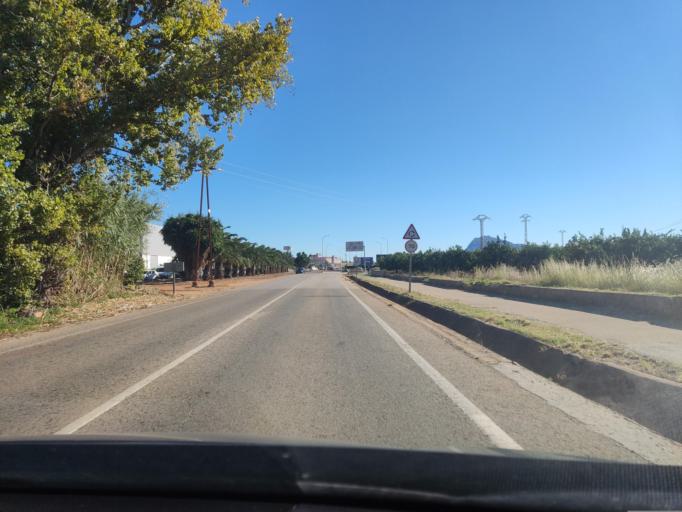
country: ES
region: Valencia
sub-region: Provincia de Alicante
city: Vergel
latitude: 38.8532
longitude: -0.0009
